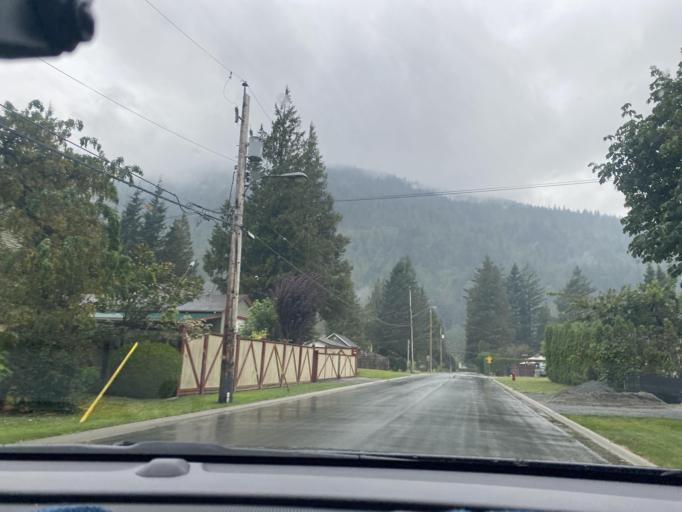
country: CA
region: British Columbia
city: Agassiz
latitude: 49.2942
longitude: -121.7777
